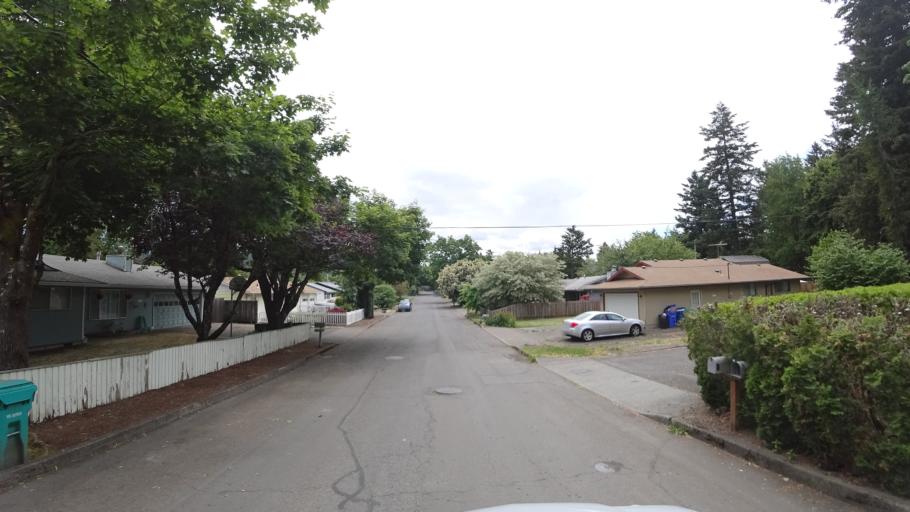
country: US
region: Oregon
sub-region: Multnomah County
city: Lents
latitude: 45.5004
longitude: -122.5193
